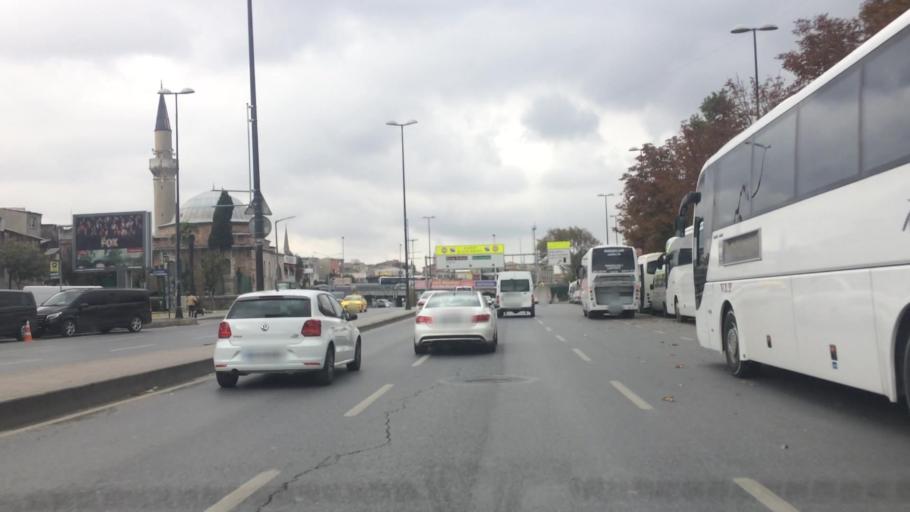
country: TR
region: Istanbul
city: Eminoenue
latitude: 41.0211
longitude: 28.9630
